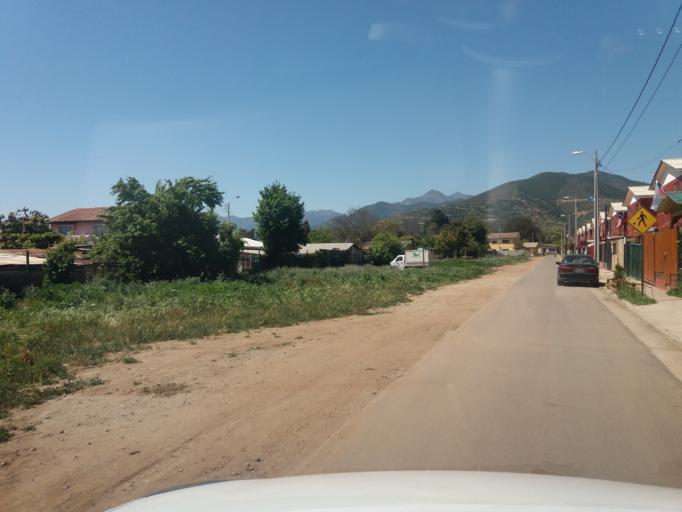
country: CL
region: Valparaiso
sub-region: Provincia de Quillota
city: Quillota
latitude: -32.9384
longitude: -71.2796
